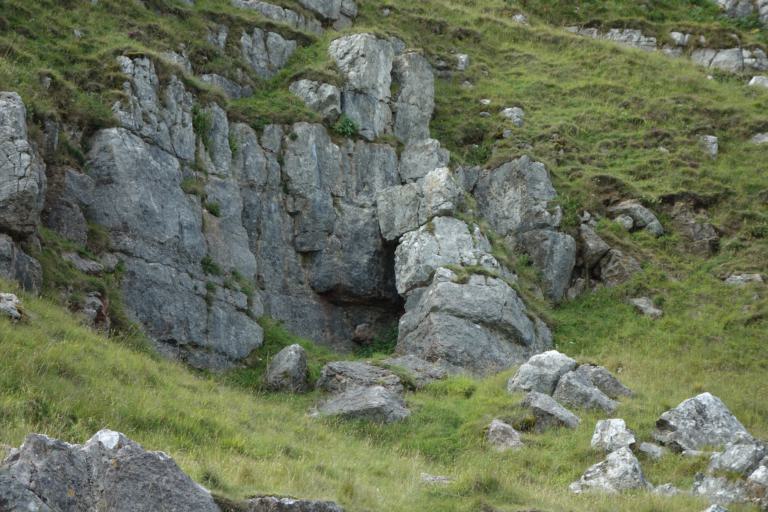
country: GB
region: Wales
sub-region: Conwy
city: Llandudno
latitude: 53.3411
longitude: -3.8670
